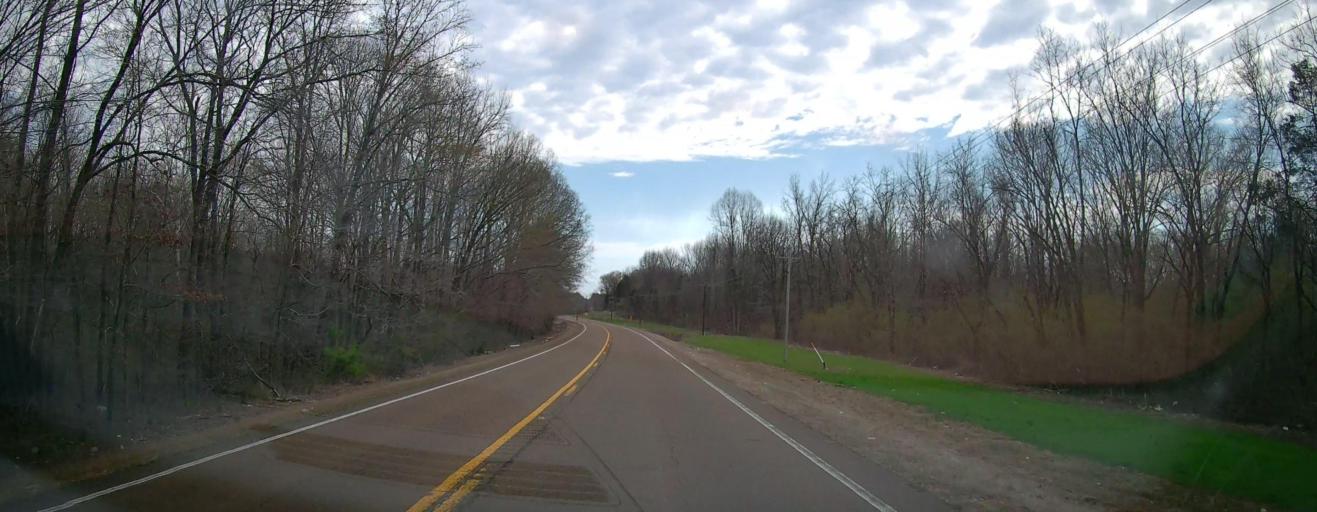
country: US
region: Mississippi
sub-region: Marshall County
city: Byhalia
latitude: 34.8490
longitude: -89.6281
